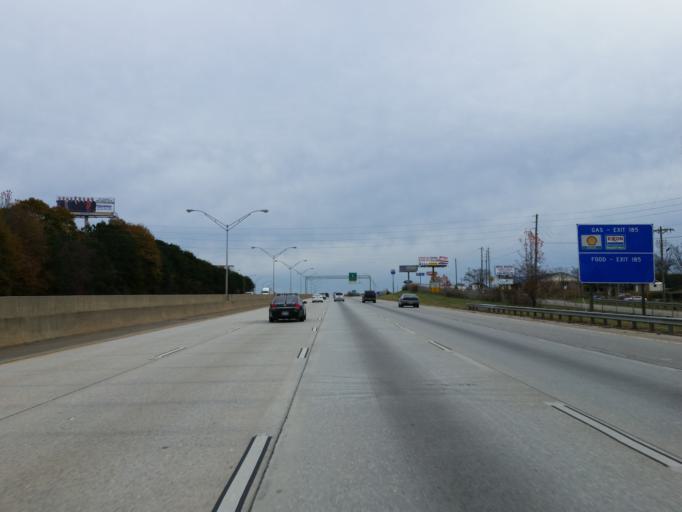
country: US
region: Georgia
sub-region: Monroe County
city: Forsyth
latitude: 33.0321
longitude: -83.9169
